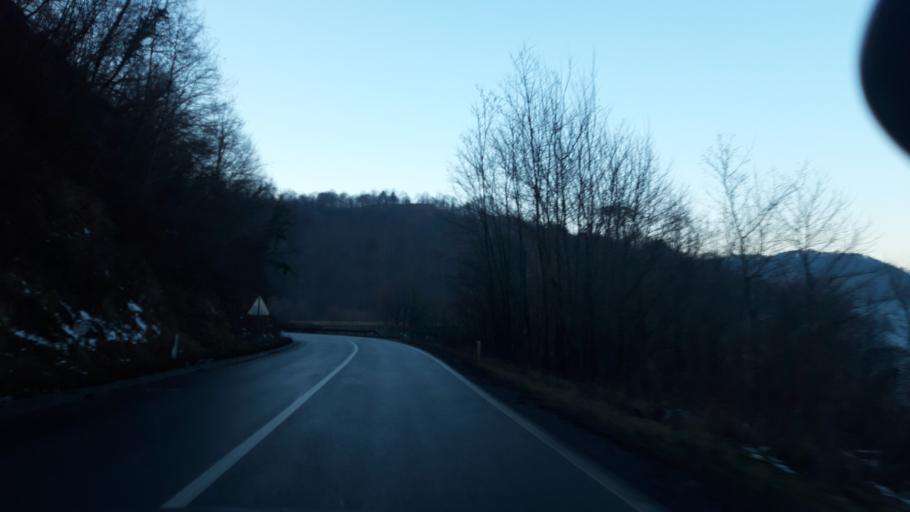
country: RS
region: Central Serbia
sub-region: Macvanski Okrug
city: Mali Zvornik
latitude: 44.3179
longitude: 19.1275
